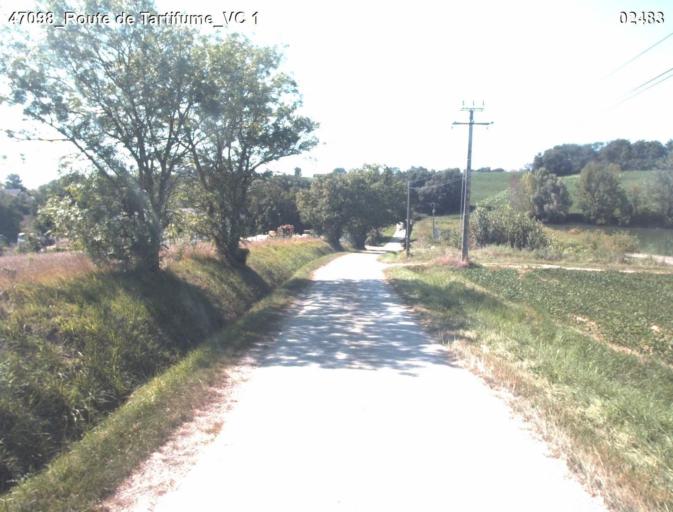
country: FR
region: Aquitaine
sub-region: Departement du Lot-et-Garonne
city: Nerac
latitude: 44.0919
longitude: 0.4065
